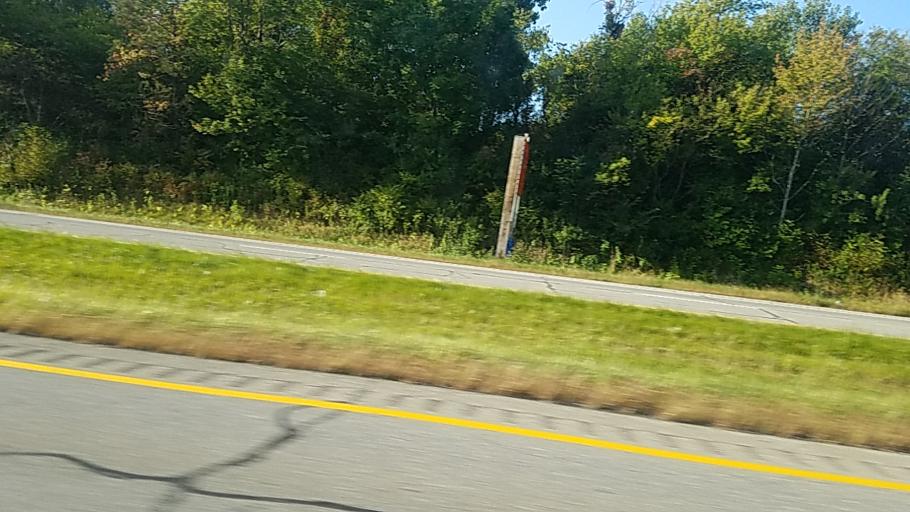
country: US
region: Ohio
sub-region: Trumbull County
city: Girard
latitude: 41.1210
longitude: -80.7026
